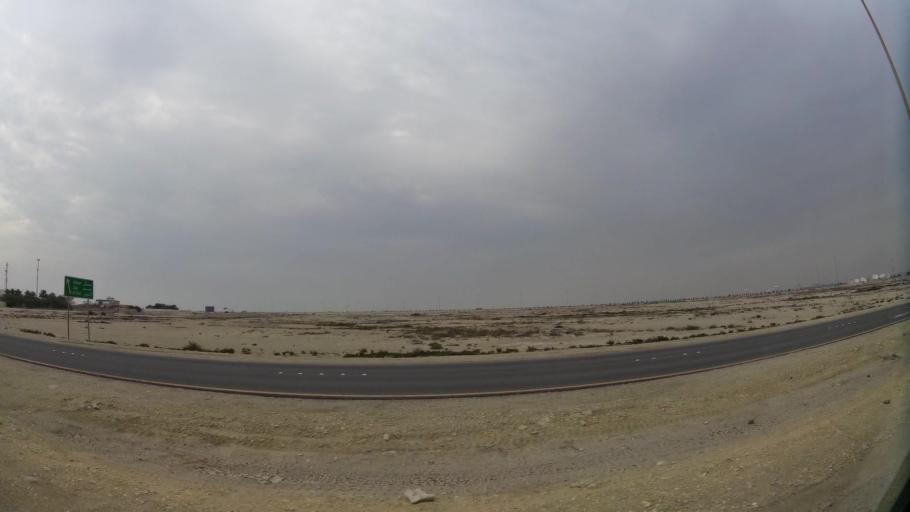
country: BH
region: Northern
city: Ar Rifa'
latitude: 26.0638
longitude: 50.6169
